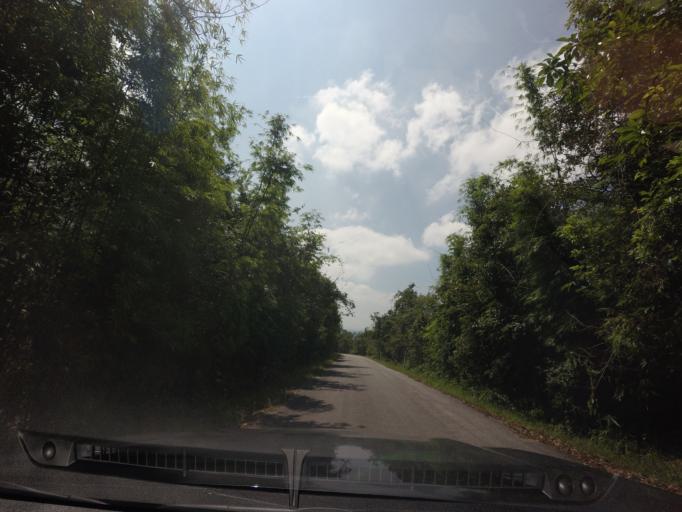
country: TH
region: Loei
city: Na Haeo
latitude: 17.4938
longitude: 100.9390
